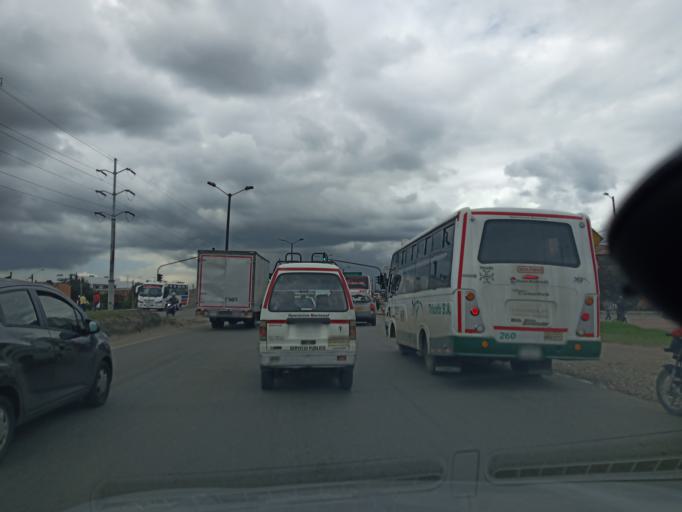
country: CO
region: Cundinamarca
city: Funza
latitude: 4.6688
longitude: -74.1512
